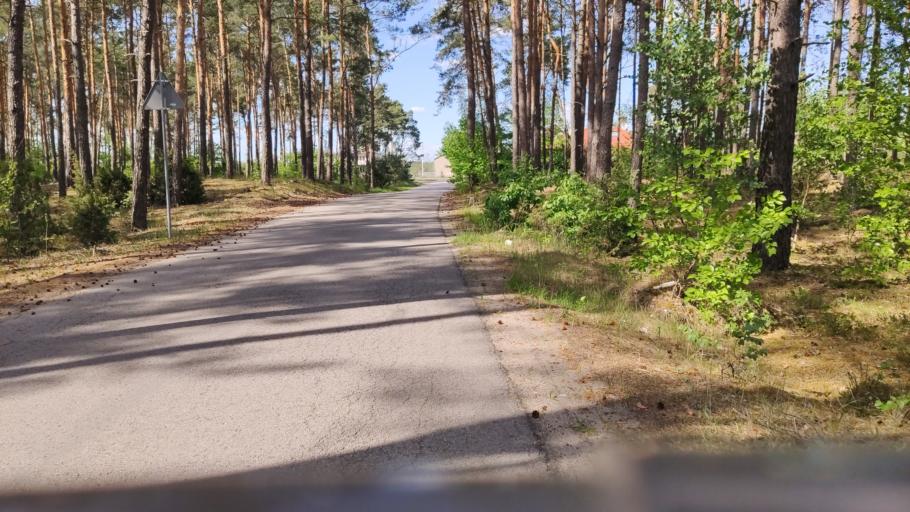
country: PL
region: Kujawsko-Pomorskie
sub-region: Wloclawek
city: Wloclawek
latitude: 52.6016
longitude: 19.0811
